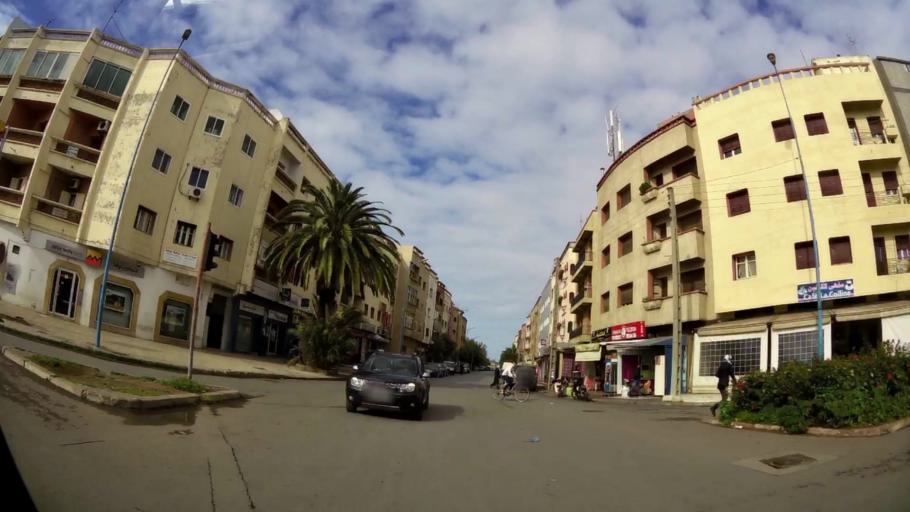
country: MA
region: Grand Casablanca
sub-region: Mohammedia
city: Mohammedia
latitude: 33.6906
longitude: -7.3826
